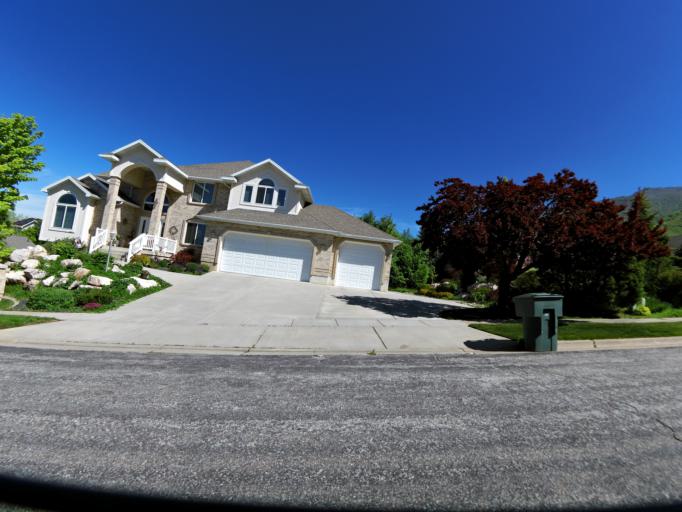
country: US
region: Utah
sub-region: Weber County
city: Uintah
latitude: 41.1678
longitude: -111.9288
